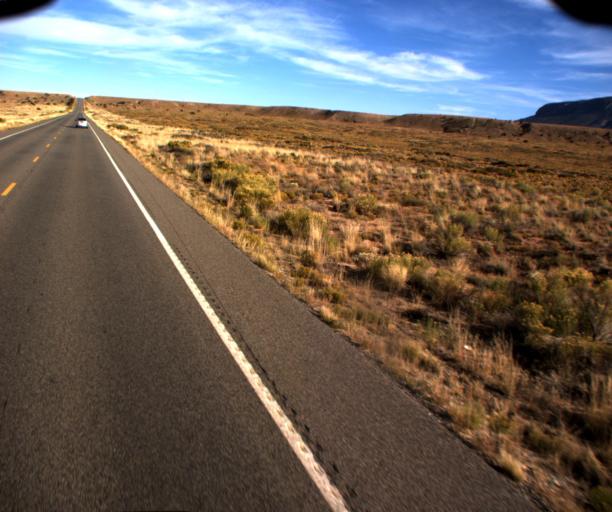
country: US
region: Arizona
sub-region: Apache County
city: Lukachukai
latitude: 36.9291
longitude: -109.2073
